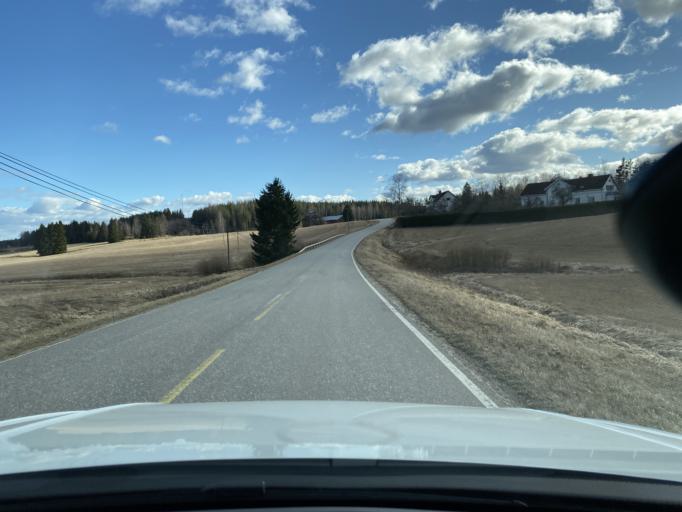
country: FI
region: Pirkanmaa
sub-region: Lounais-Pirkanmaa
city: Punkalaidun
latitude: 61.0669
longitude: 23.1804
